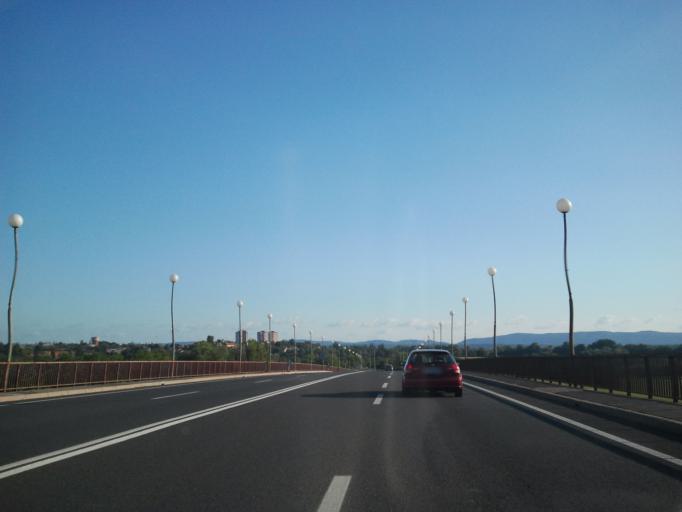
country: HR
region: Sisacko-Moslavacka
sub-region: Grad Sisak
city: Sisak
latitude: 45.4920
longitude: 16.3666
